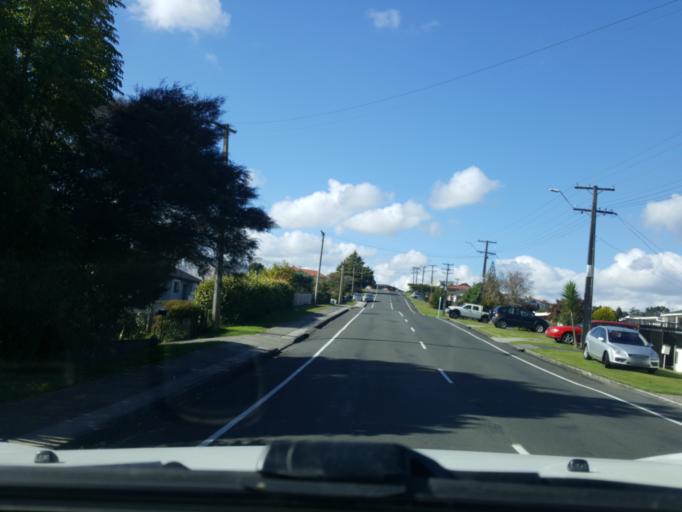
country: NZ
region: Waikato
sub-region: Waikato District
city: Ngaruawahia
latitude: -37.5477
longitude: 175.1652
